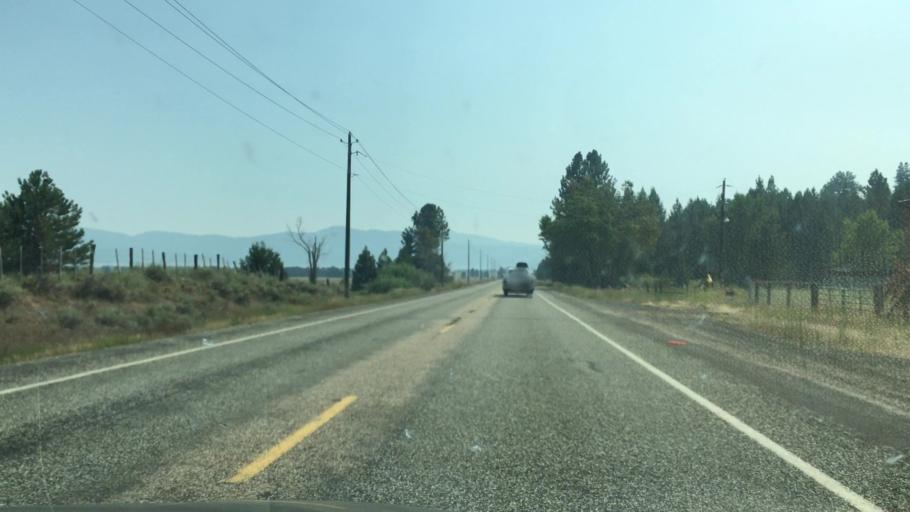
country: US
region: Idaho
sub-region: Valley County
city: Cascade
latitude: 44.3642
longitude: -116.0194
